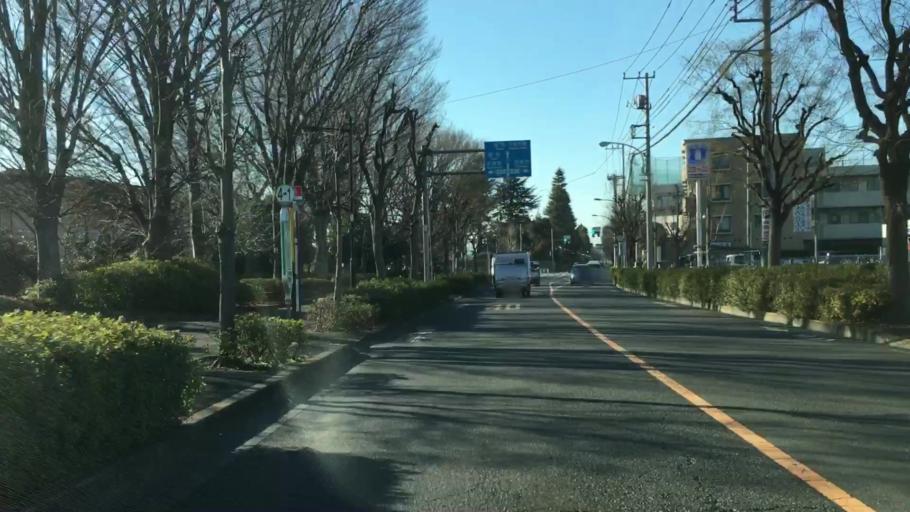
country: JP
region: Tokyo
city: Musashino
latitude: 35.7086
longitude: 139.5538
